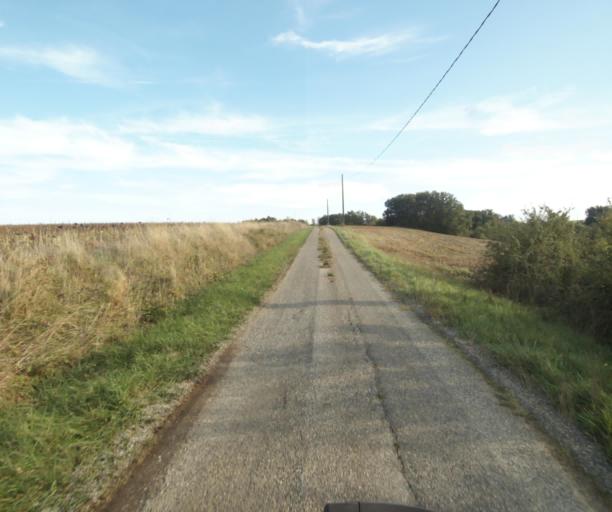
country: FR
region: Midi-Pyrenees
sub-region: Departement du Tarn-et-Garonne
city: Finhan
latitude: 43.9153
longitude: 1.1092
